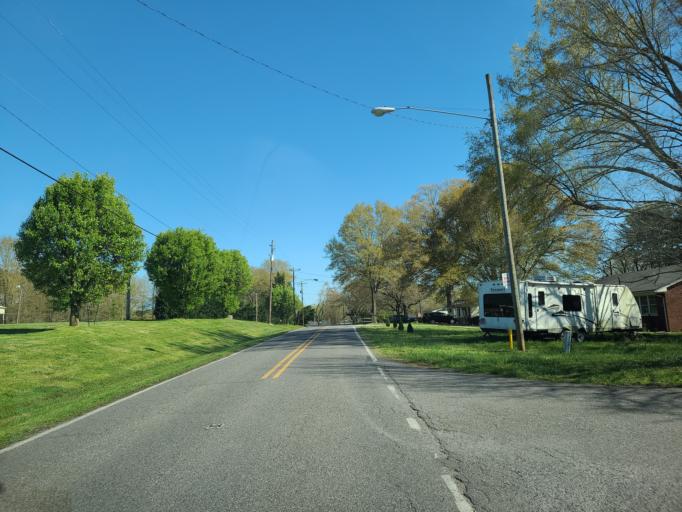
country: US
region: North Carolina
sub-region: Cleveland County
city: Shelby
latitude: 35.2748
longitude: -81.5643
